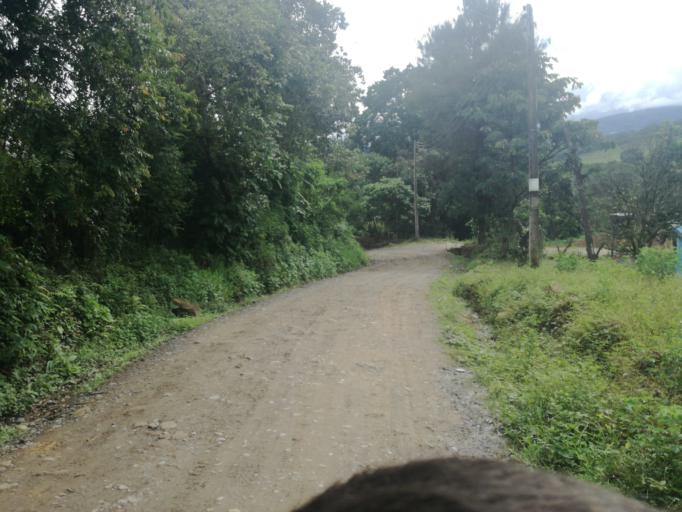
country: CO
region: Boyaca
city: Santana
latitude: 6.0631
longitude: -73.4836
